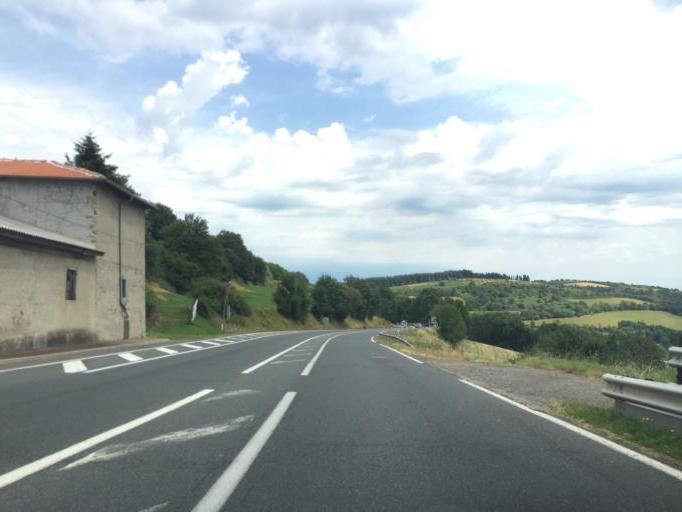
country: FR
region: Rhone-Alpes
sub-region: Departement du Rhone
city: Amplepuis
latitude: 45.9153
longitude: 4.3460
